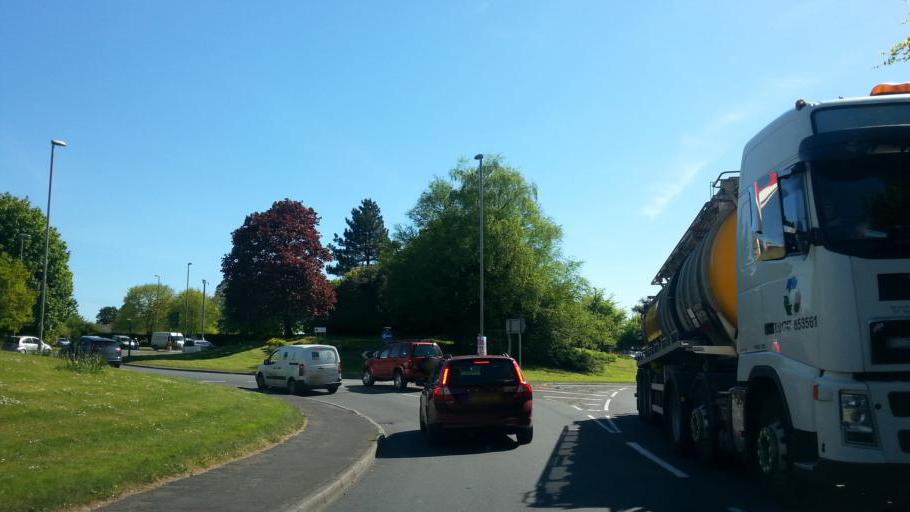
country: GB
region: England
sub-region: Dorset
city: Shaftesbury
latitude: 51.0106
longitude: -2.1931
